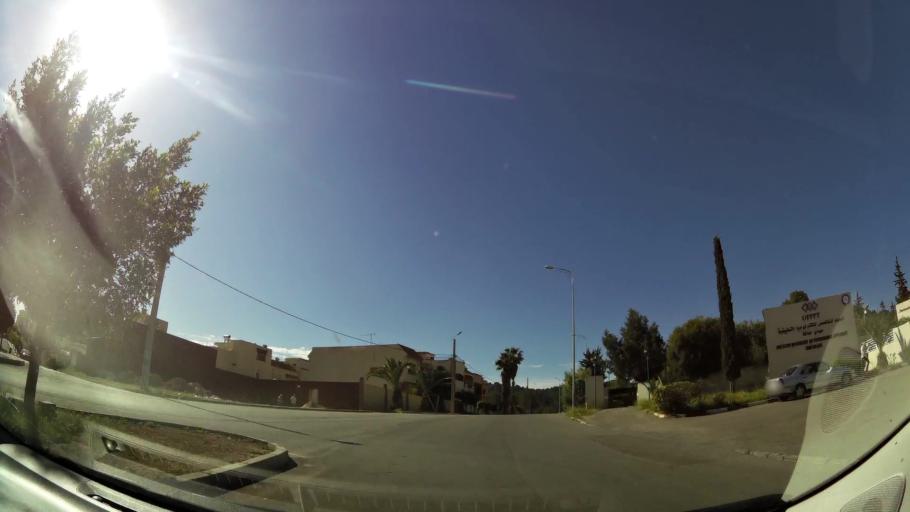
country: MA
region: Oriental
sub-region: Oujda-Angad
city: Oujda
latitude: 34.6487
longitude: -1.8935
